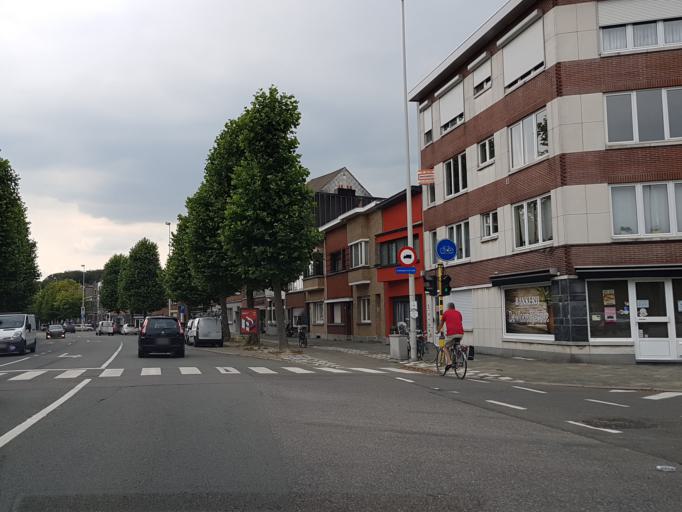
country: BE
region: Flanders
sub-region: Provincie Antwerpen
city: Borsbeek
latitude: 51.1965
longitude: 4.4592
